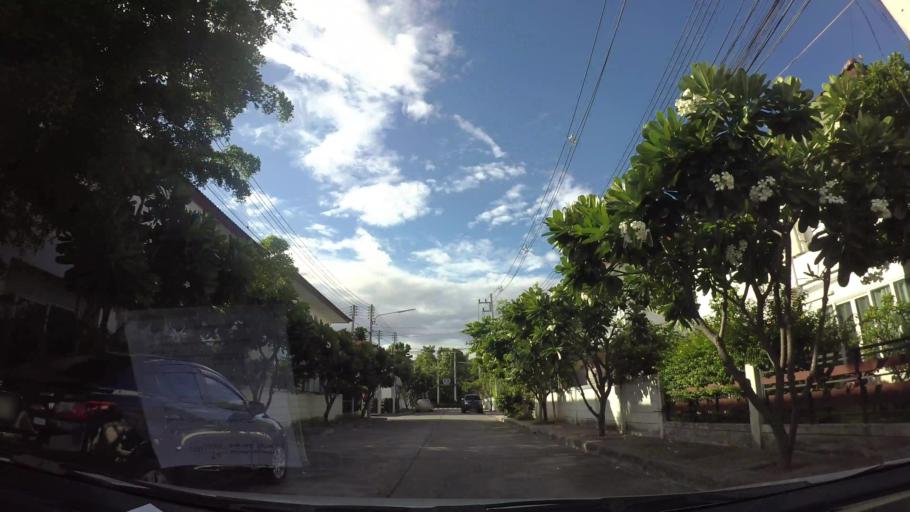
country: TH
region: Chiang Mai
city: Saraphi
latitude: 18.7556
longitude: 99.0281
